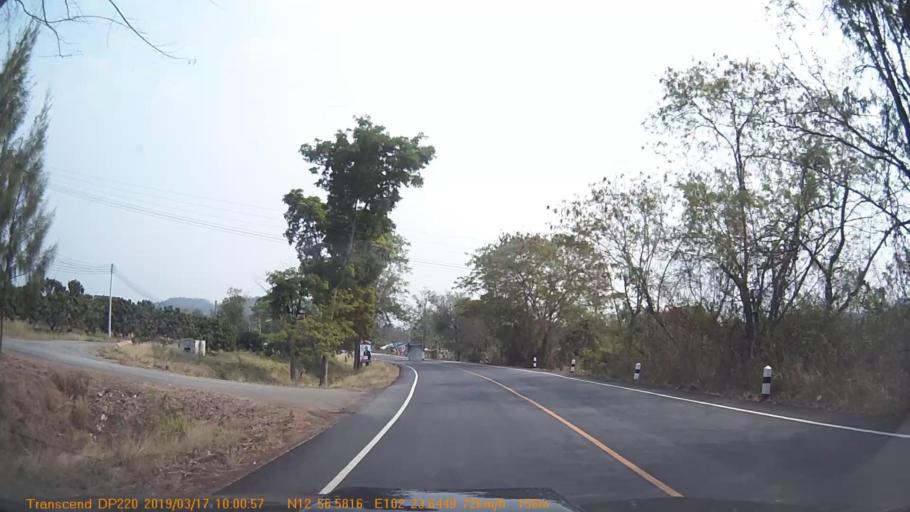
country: TH
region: Chanthaburi
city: Pong Nam Ron
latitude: 12.9450
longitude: 102.3949
